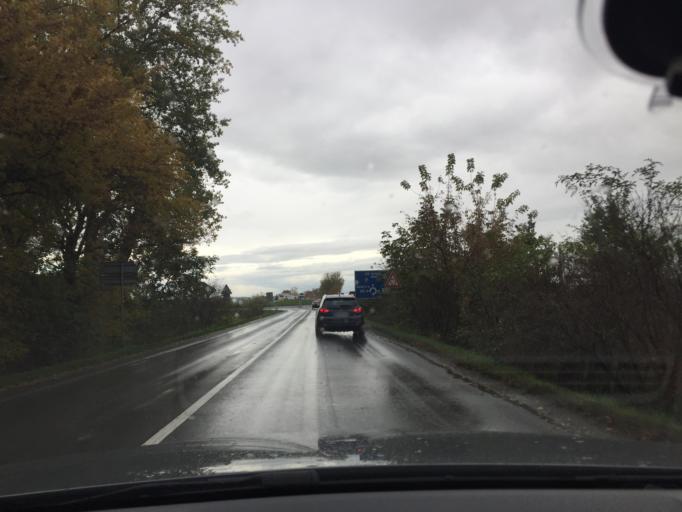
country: CZ
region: Central Bohemia
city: Odolena Voda
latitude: 50.2435
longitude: 14.3662
